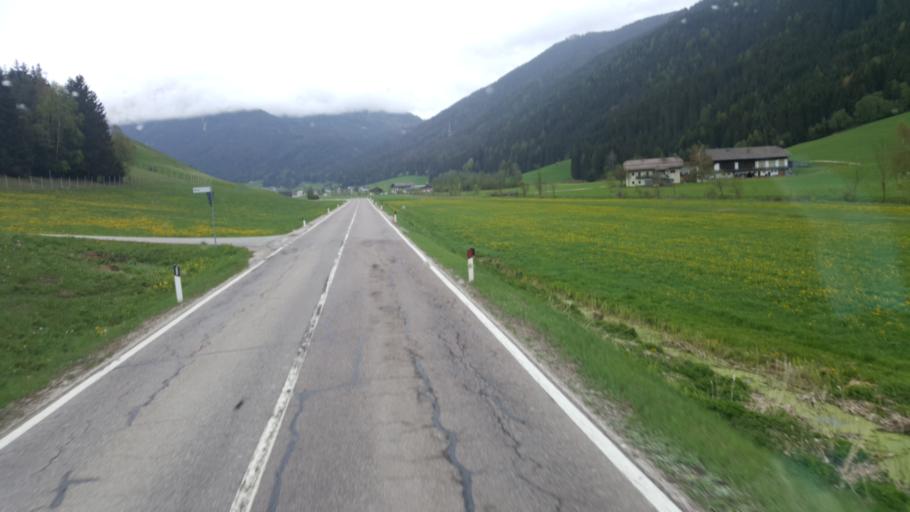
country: IT
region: Trentino-Alto Adige
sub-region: Bolzano
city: Valle di Casies - Gsies
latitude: 46.7663
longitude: 12.1567
